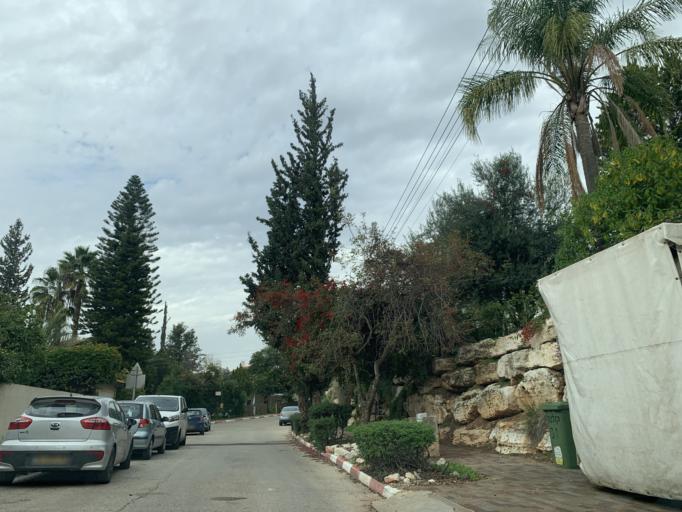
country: IL
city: Nirit
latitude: 32.1456
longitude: 34.9836
